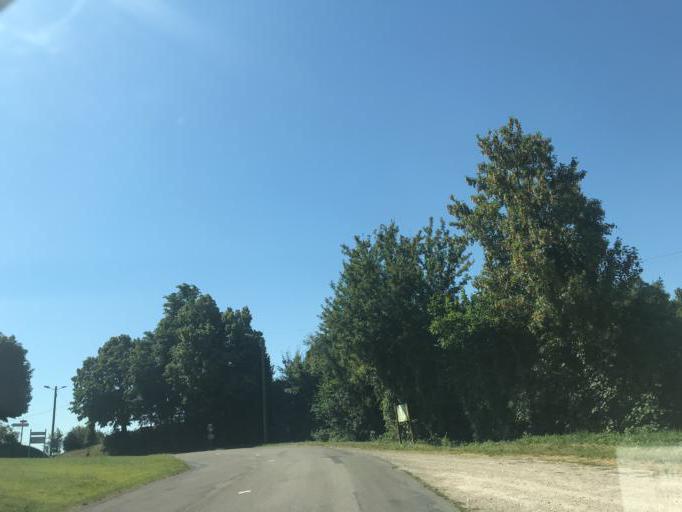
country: FR
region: Rhone-Alpes
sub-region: Departement de l'Ain
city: Saint-Martin-du-Mont
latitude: 46.1004
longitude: 5.3272
